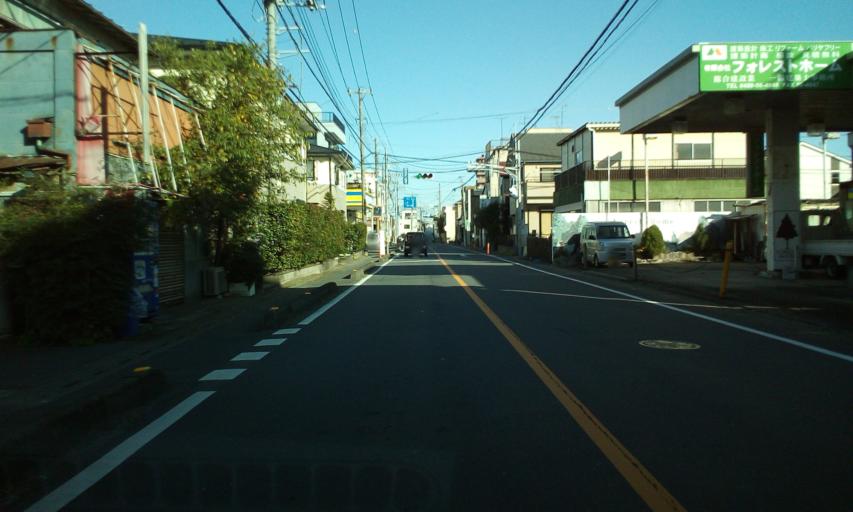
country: JP
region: Chiba
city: Matsudo
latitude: 35.7870
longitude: 139.8845
